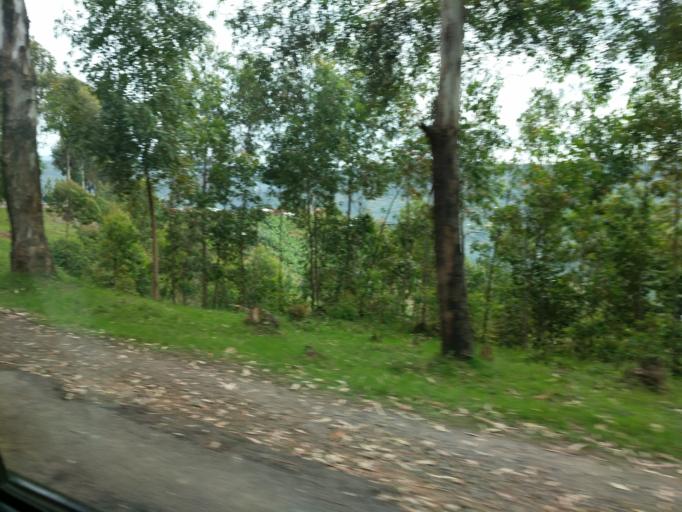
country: RW
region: Kigali
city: Kigali
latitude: -1.7902
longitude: 29.9302
